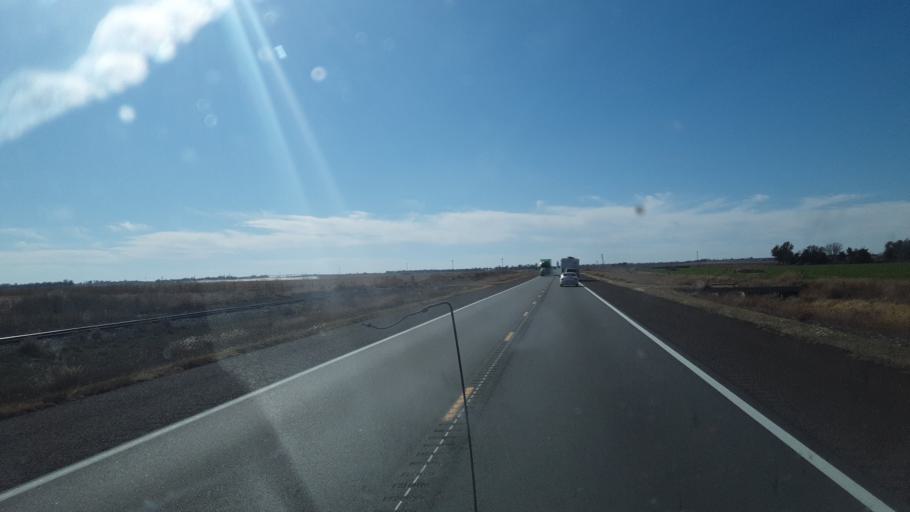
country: US
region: Kansas
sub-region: Barton County
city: Great Bend
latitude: 38.2870
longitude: -98.9344
